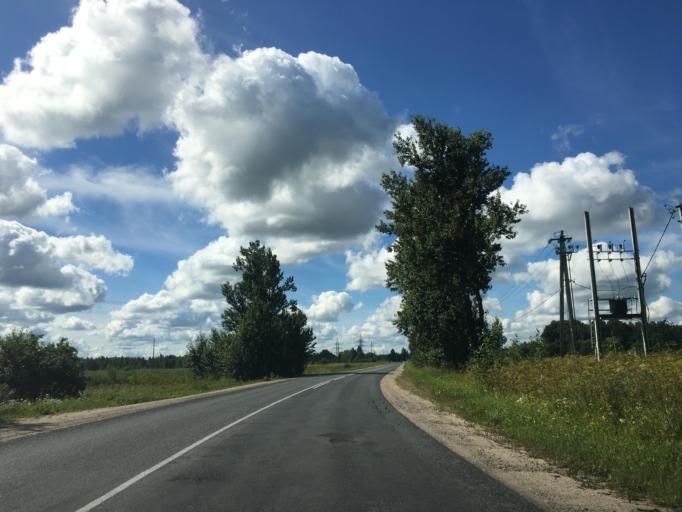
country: RU
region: Pskov
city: Pskov
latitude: 57.7793
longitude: 28.1682
